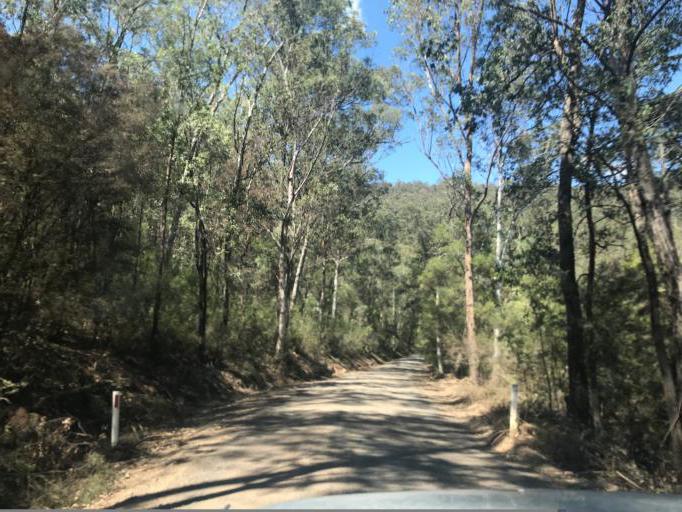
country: AU
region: New South Wales
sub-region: Wyong Shire
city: Little Jilliby
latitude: -33.1789
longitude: 151.0590
